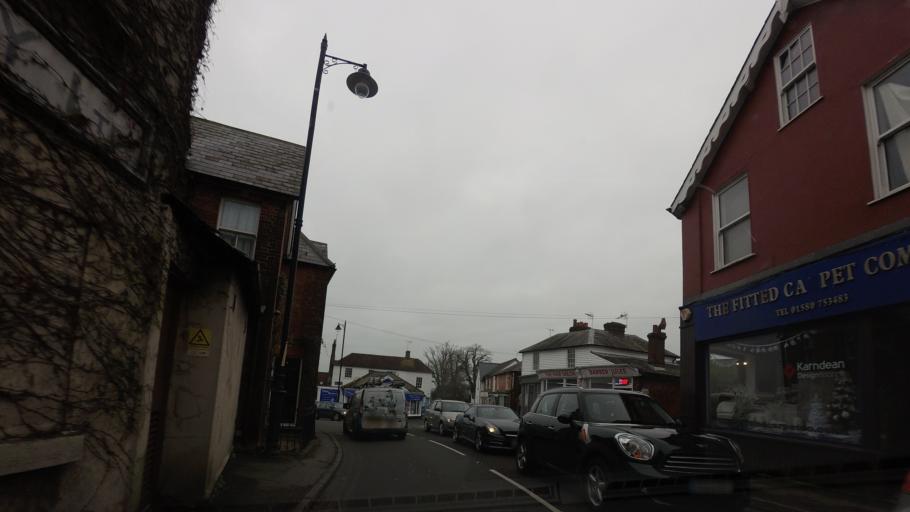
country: GB
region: England
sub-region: Kent
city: Hawkhurst
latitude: 51.0478
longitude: 0.5104
